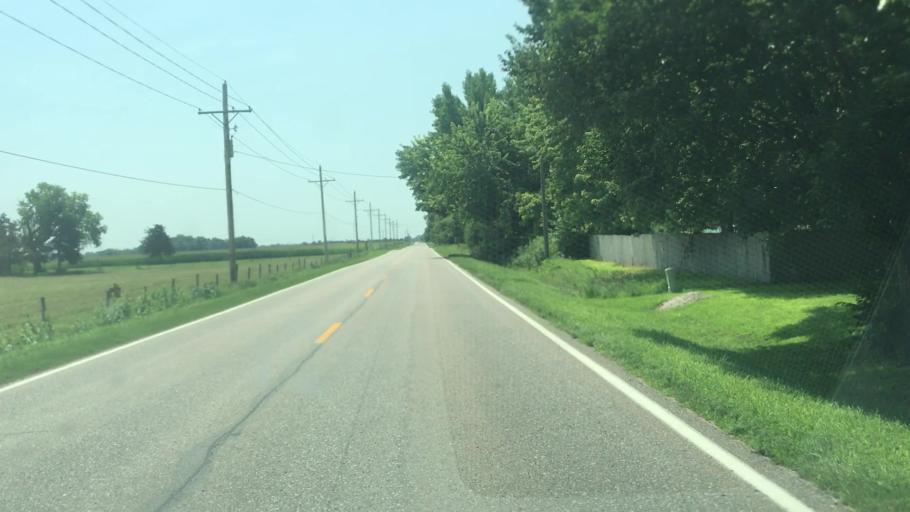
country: US
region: Nebraska
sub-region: Hall County
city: Grand Island
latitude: 40.8932
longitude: -98.3017
